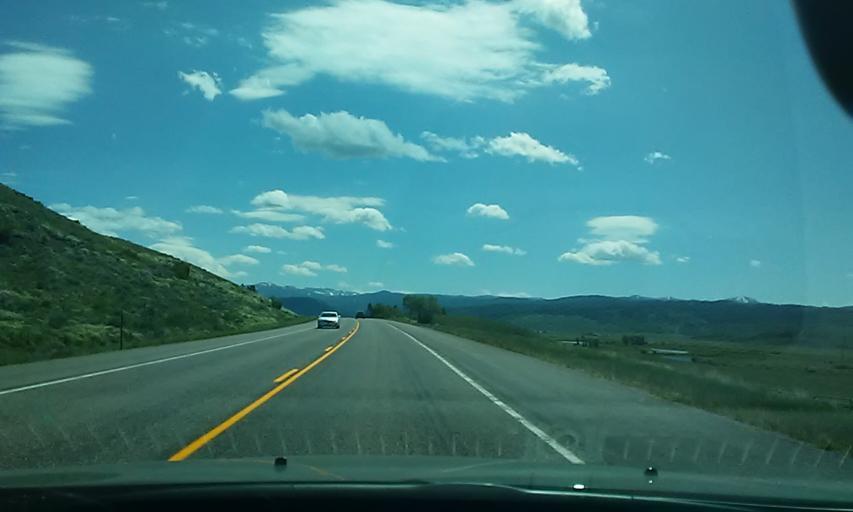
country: US
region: Wyoming
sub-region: Teton County
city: Jackson
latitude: 43.8393
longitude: -110.4496
